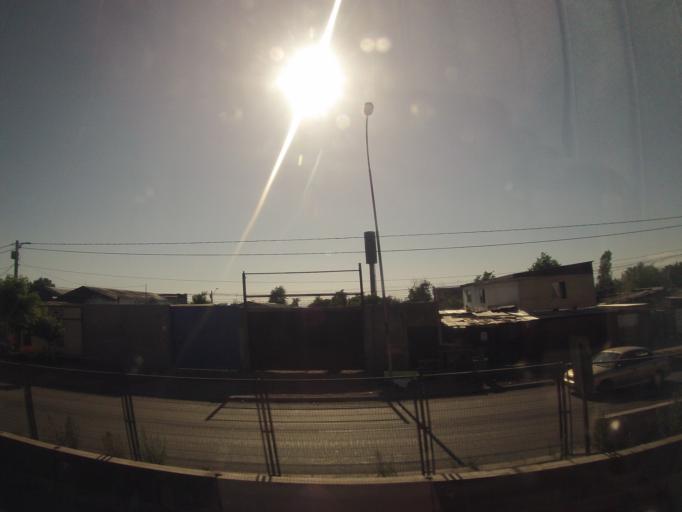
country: CL
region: Santiago Metropolitan
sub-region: Provincia de Santiago
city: Santiago
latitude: -33.4688
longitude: -70.6882
